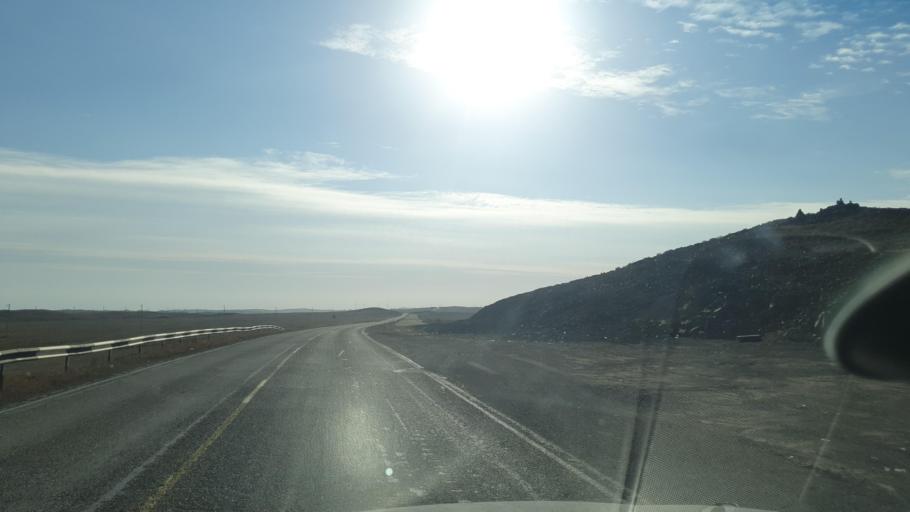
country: KZ
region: Zhambyl
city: Mynaral
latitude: 45.7313
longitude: 73.4054
